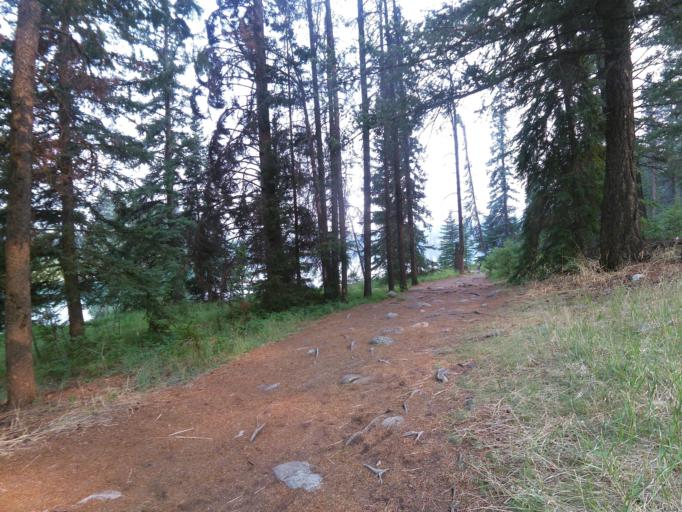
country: CA
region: Alberta
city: Jasper Park Lodge
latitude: 52.8805
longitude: -118.0550
